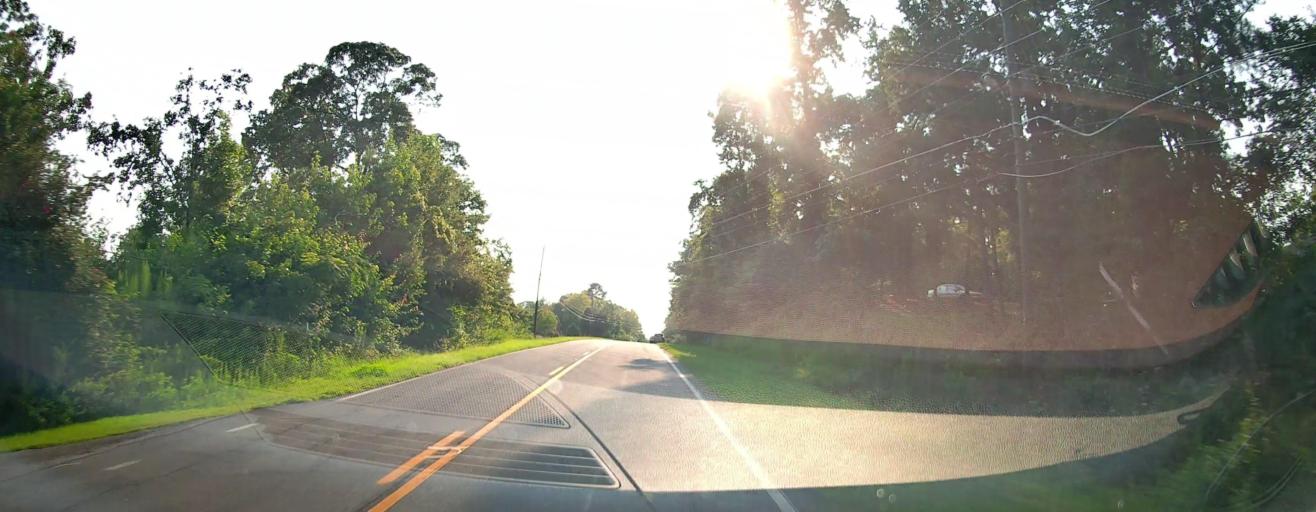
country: US
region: Georgia
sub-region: Bibb County
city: West Point
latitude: 32.8315
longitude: -83.8022
